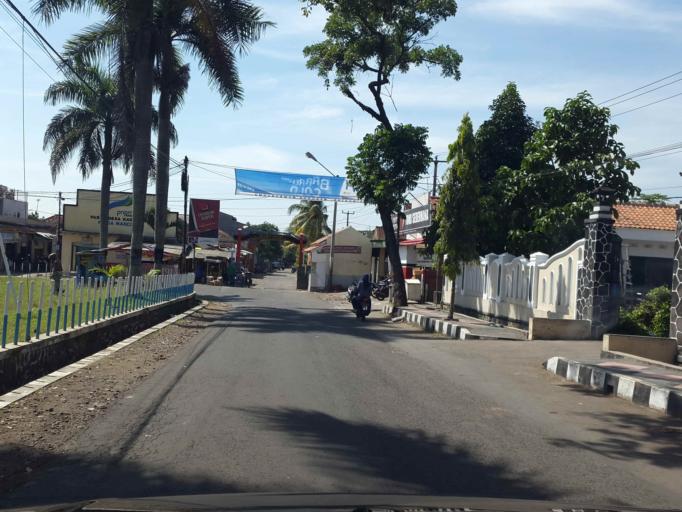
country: ID
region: West Java
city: Ciranjang-hilir
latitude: -6.7688
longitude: 107.2031
